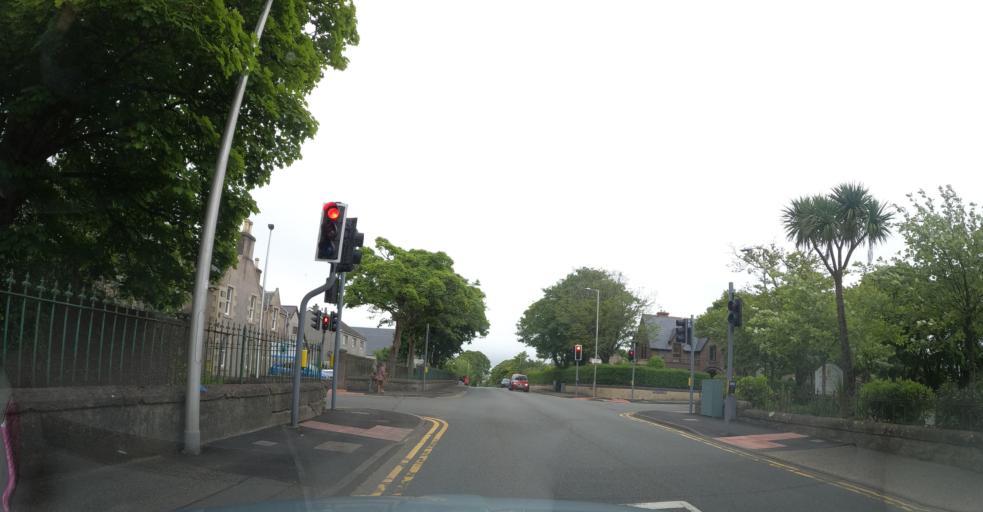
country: GB
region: Scotland
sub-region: Eilean Siar
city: Stornoway
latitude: 58.2109
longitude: -6.3825
